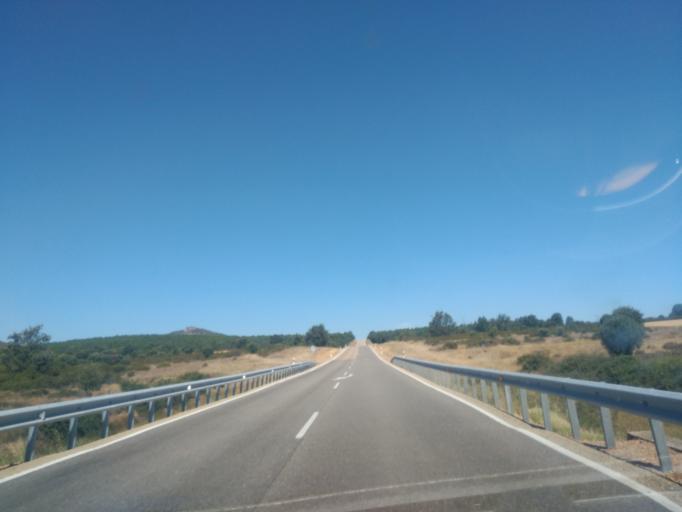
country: ES
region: Castille and Leon
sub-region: Provincia de Zamora
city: Tabara
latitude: 41.8606
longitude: -5.9963
